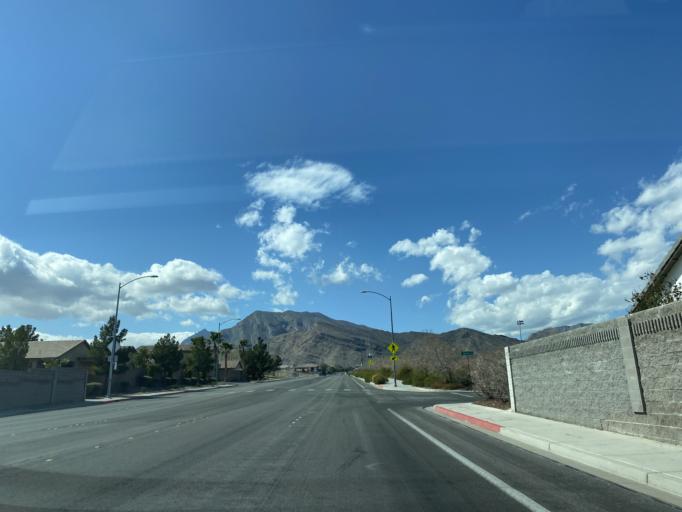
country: US
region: Nevada
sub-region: Clark County
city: Summerlin South
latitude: 36.2259
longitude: -115.3081
